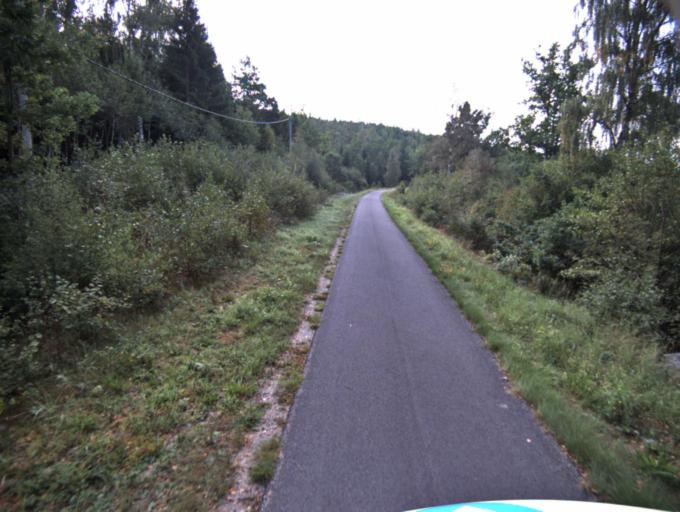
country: SE
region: Vaestra Goetaland
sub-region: Ulricehamns Kommun
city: Ulricehamn
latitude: 57.7021
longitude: 13.3942
